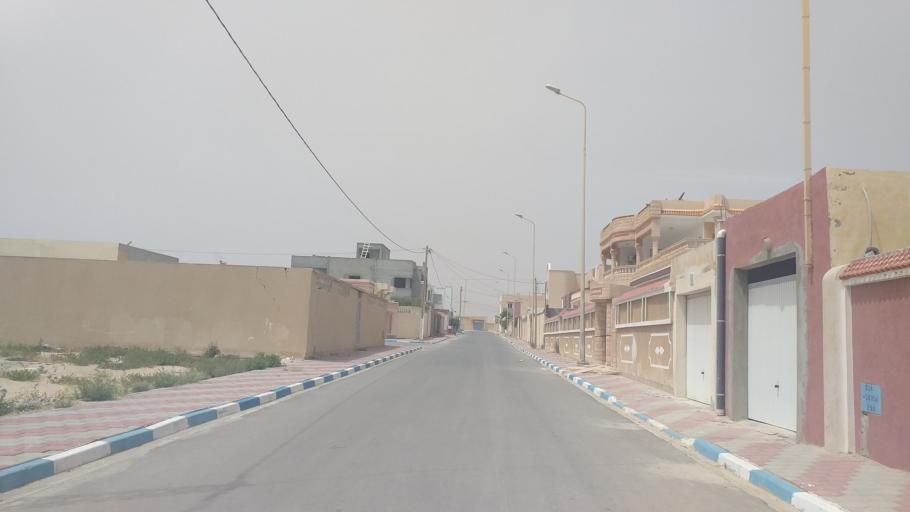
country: TN
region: Qabis
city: Gabes
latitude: 33.9525
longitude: 10.0702
